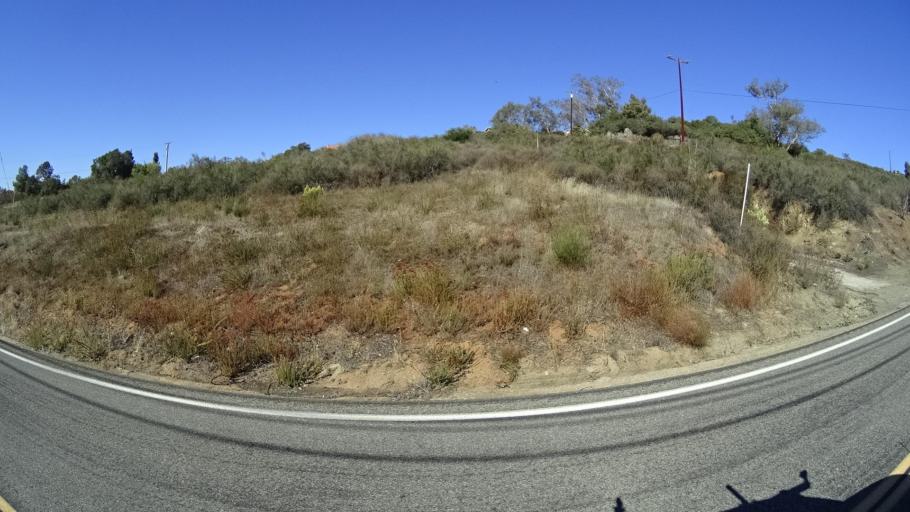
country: US
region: California
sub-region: San Diego County
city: Jamul
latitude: 32.6935
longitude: -116.7476
